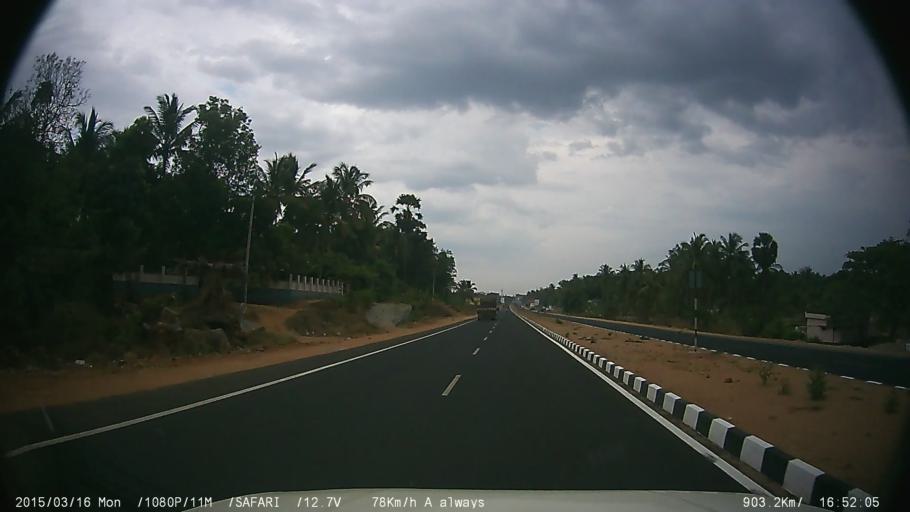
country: IN
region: Kerala
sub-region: Palakkad district
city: Palakkad
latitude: 10.6415
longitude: 76.5291
